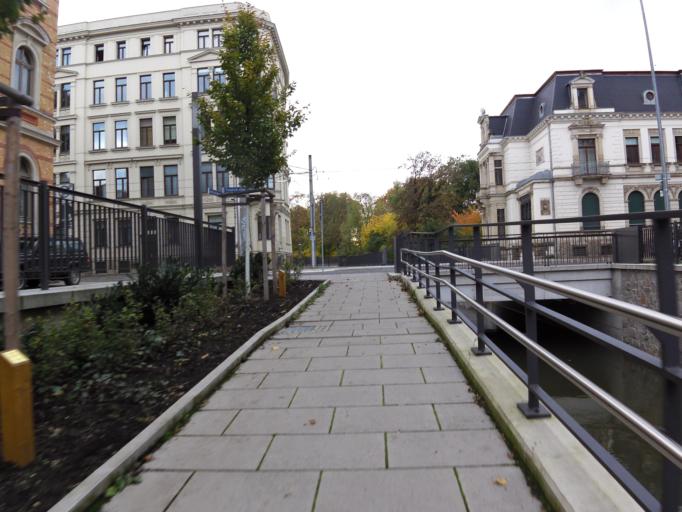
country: DE
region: Saxony
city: Leipzig
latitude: 51.3405
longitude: 12.3609
